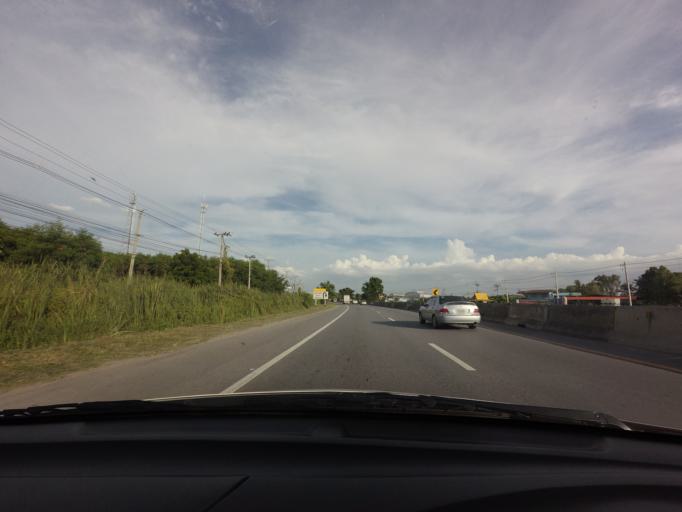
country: TH
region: Pathum Thani
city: Lat Lum Kaeo
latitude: 13.9934
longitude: 100.3771
